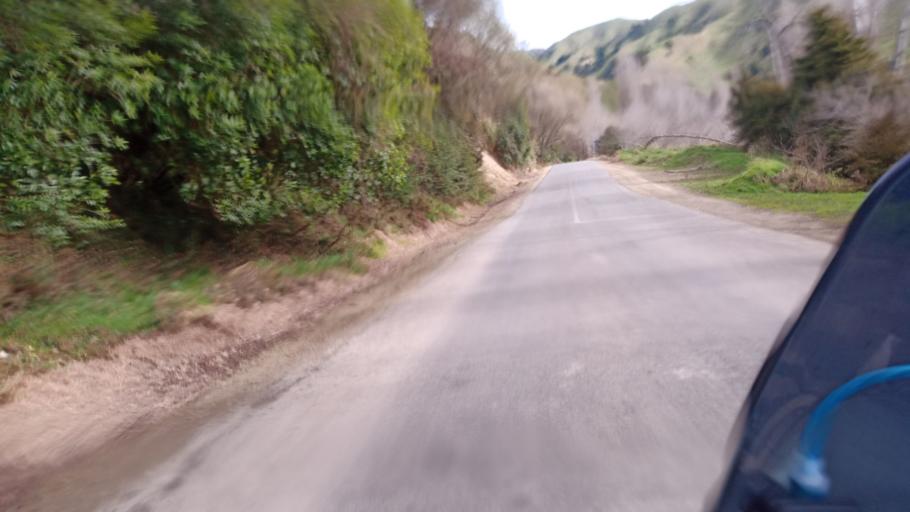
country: NZ
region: Hawke's Bay
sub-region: Wairoa District
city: Wairoa
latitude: -38.8028
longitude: 177.4499
